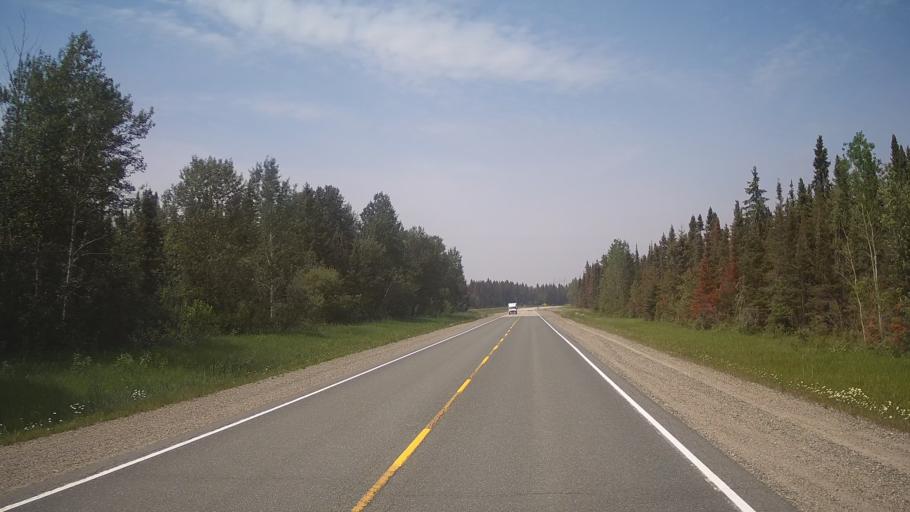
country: CA
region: Ontario
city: Timmins
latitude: 48.7272
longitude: -81.3498
